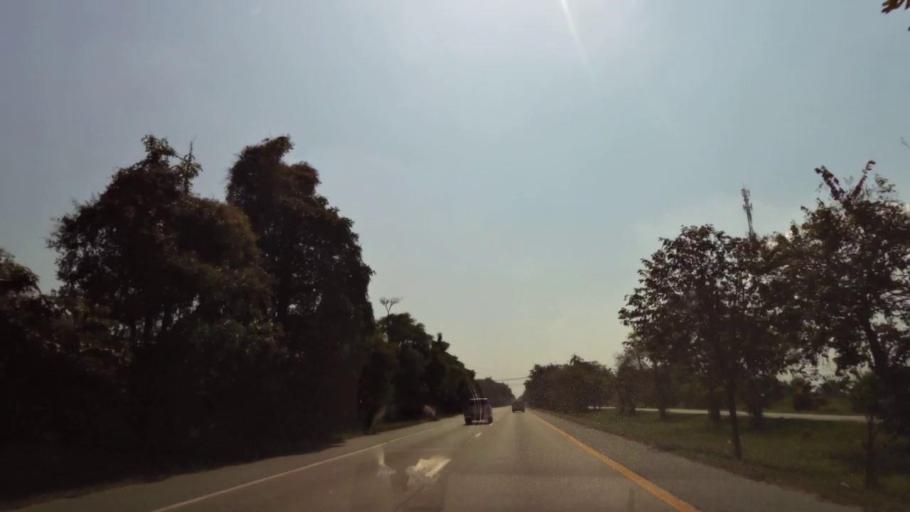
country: TH
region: Phichit
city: Wachira Barami
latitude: 16.5768
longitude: 100.1480
